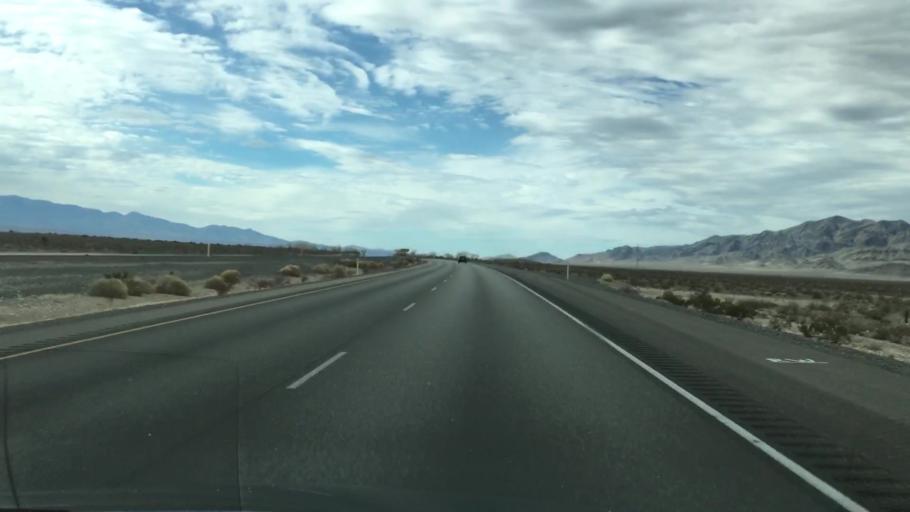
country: US
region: Nevada
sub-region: Nye County
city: Pahrump
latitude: 36.5791
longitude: -115.7074
